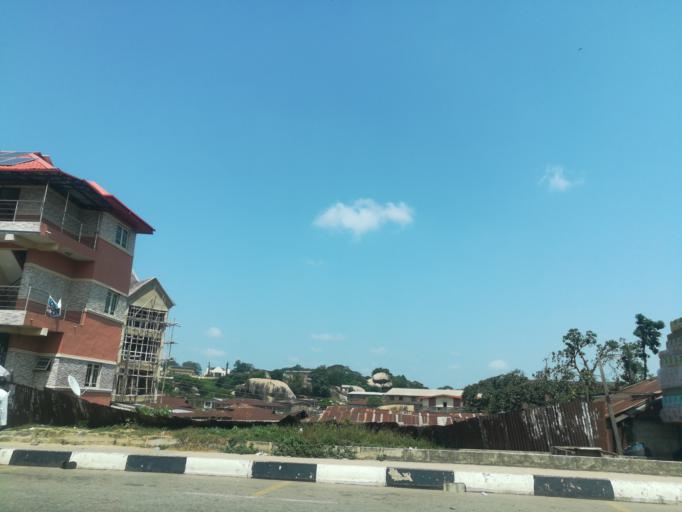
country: NG
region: Ogun
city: Abeokuta
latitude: 7.1562
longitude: 3.3444
